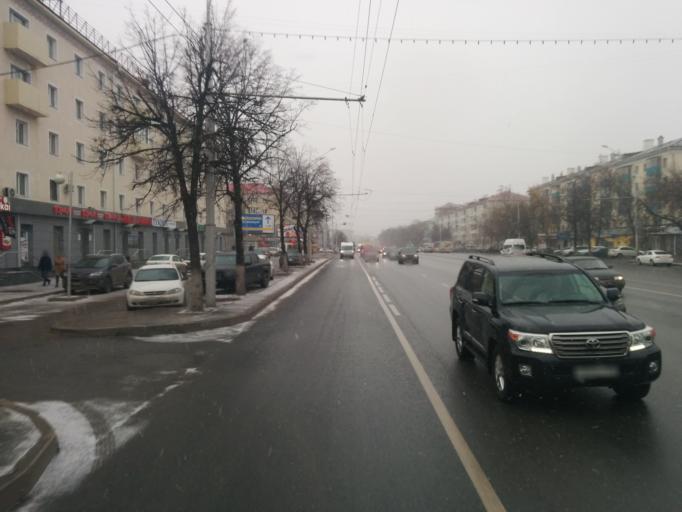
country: RU
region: Bashkortostan
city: Ufa
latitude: 54.7442
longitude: 55.9906
